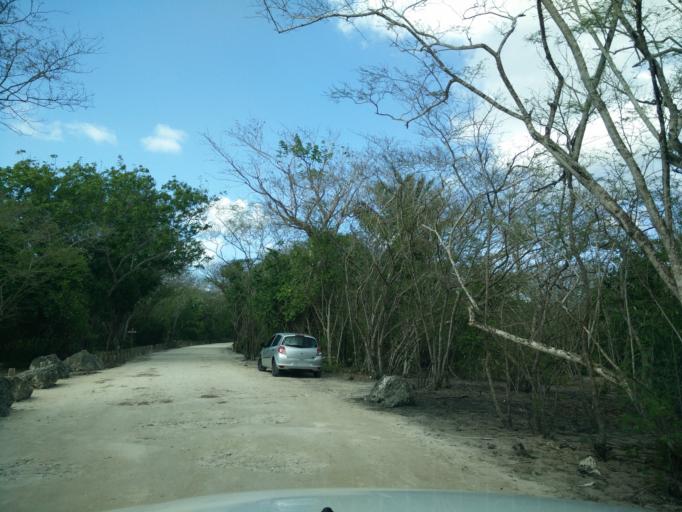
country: GP
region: Guadeloupe
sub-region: Guadeloupe
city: Port-Louis
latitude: 16.4316
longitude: -61.5369
